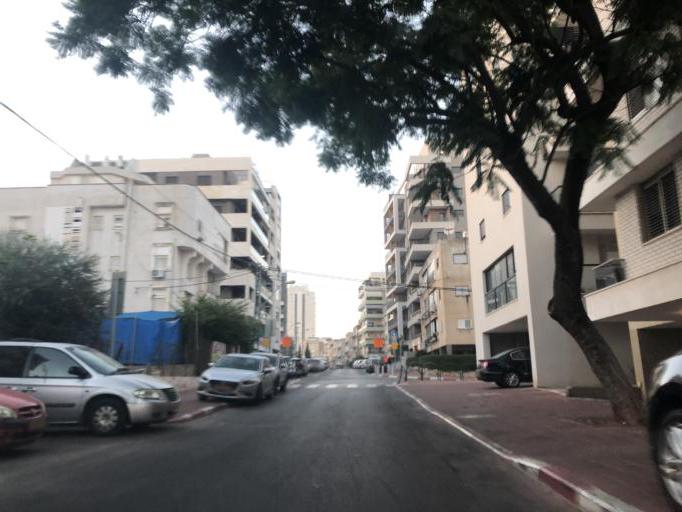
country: IL
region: Tel Aviv
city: Bene Beraq
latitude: 32.0668
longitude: 34.8275
